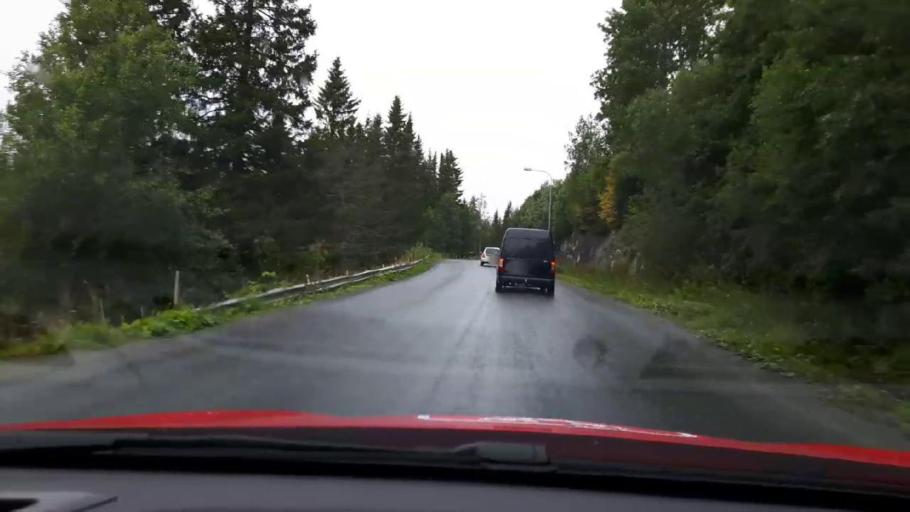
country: SE
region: Jaemtland
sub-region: Are Kommun
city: Are
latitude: 63.3827
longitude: 13.1539
